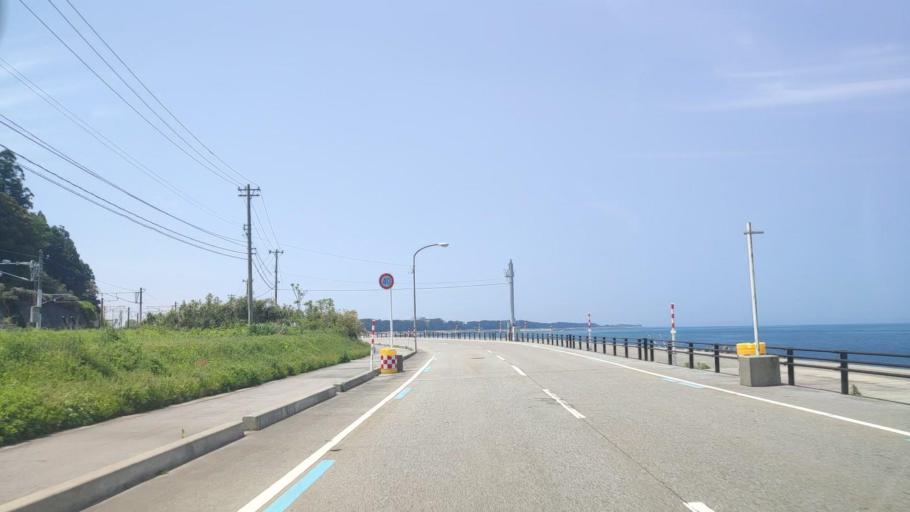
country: JP
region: Toyama
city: Nyuzen
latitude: 36.9676
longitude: 137.5793
